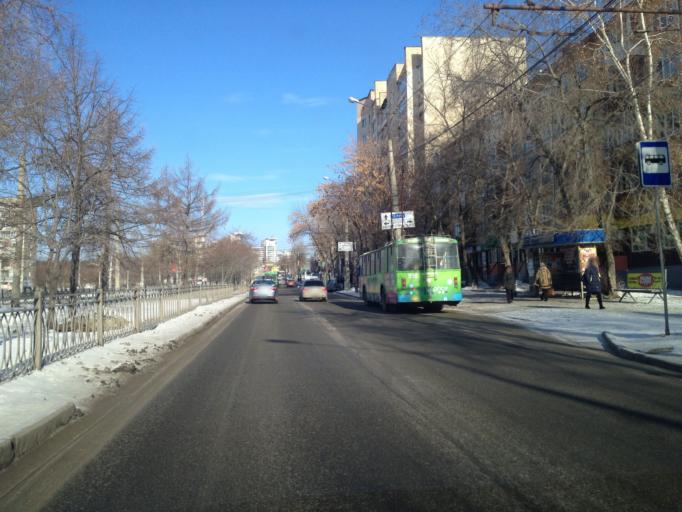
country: RU
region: Sverdlovsk
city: Yekaterinburg
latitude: 56.8220
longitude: 60.5732
